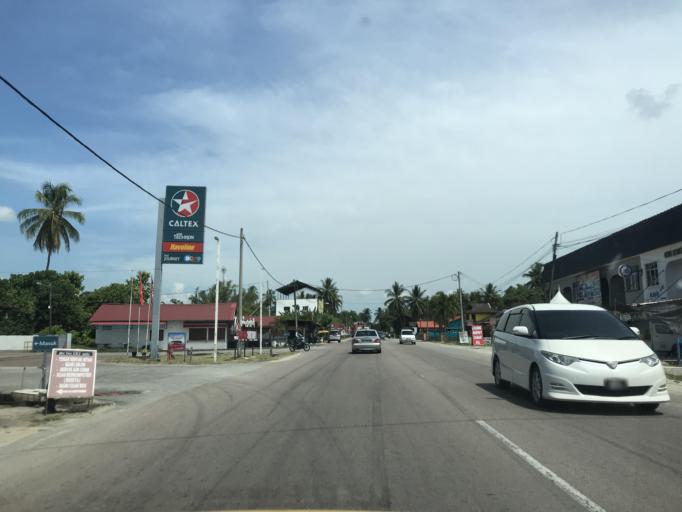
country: MY
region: Kelantan
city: Kota Bharu
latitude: 6.1192
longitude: 102.1908
